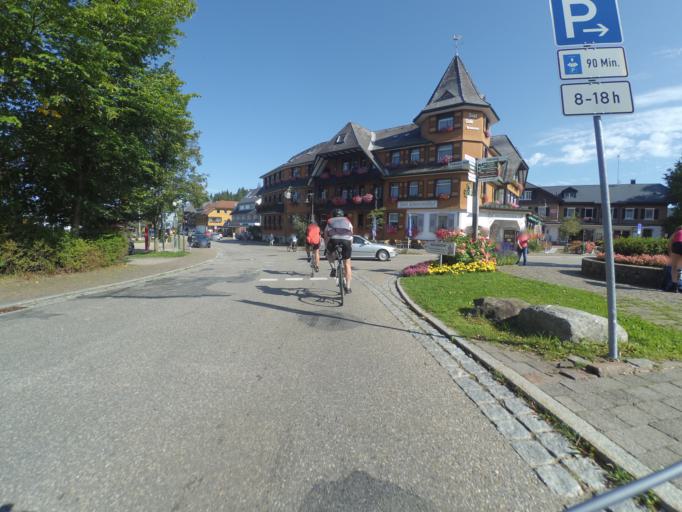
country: DE
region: Baden-Wuerttemberg
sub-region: Freiburg Region
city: Hinterzarten
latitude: 47.9055
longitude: 8.1057
